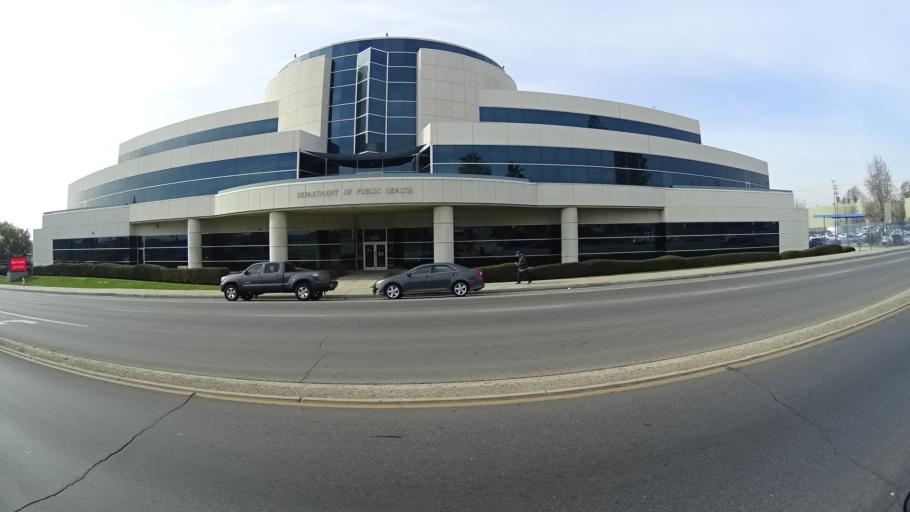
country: US
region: California
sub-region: Kern County
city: Bakersfield
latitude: 35.3837
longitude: -118.9674
